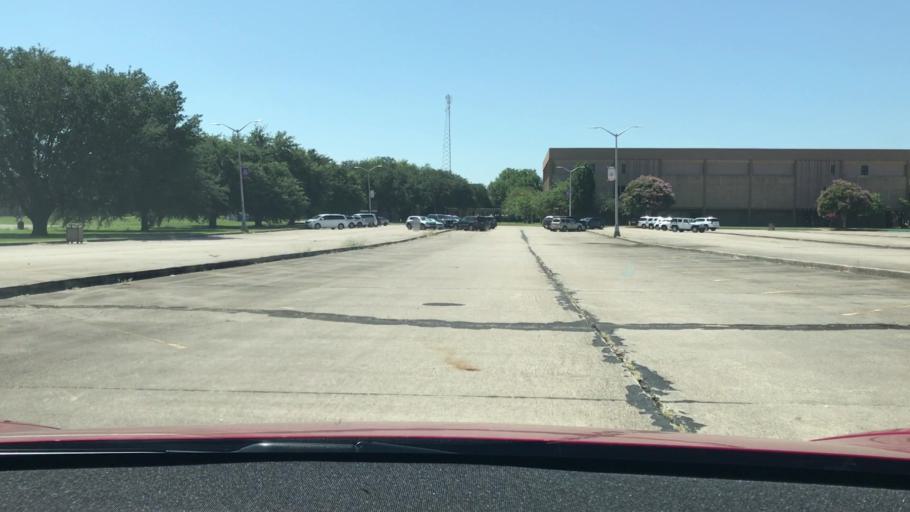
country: US
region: Louisiana
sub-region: Bossier Parish
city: Bossier City
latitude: 32.4307
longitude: -93.7053
